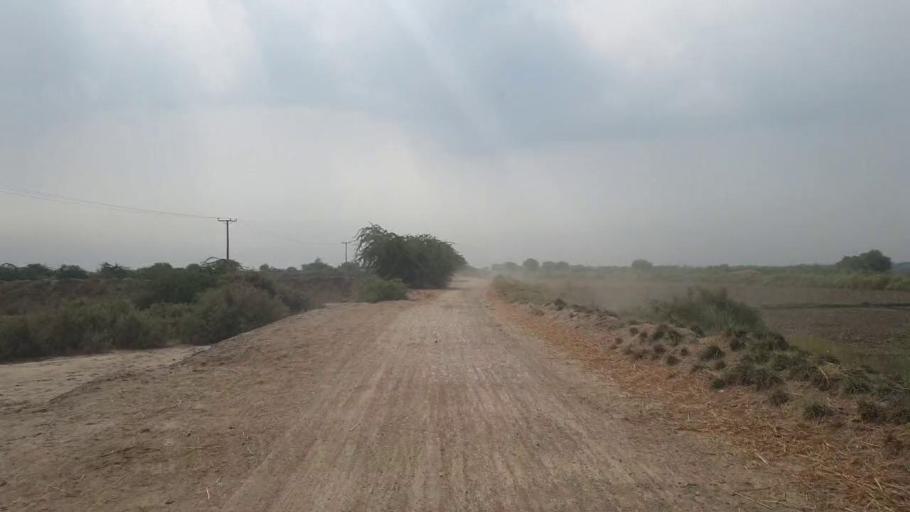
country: PK
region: Sindh
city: Talhar
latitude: 24.9330
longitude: 68.7883
